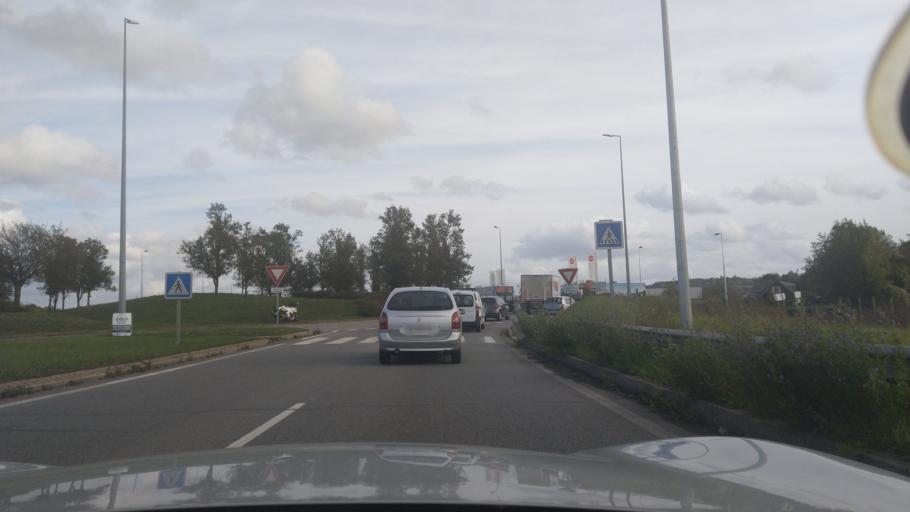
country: FR
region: Ile-de-France
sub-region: Departement des Yvelines
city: Villennes-sur-Seine
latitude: 48.9174
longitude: 2.0110
